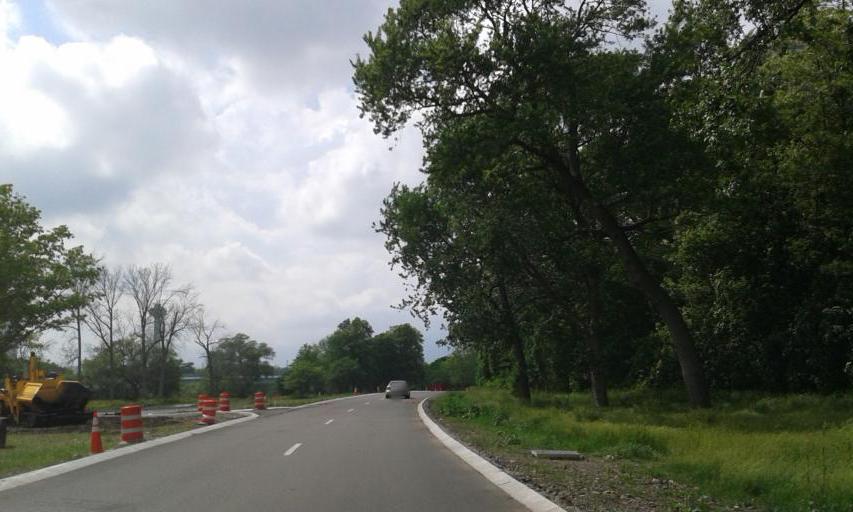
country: US
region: New York
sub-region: Niagara County
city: Niagara Falls
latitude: 43.0814
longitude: -79.0601
